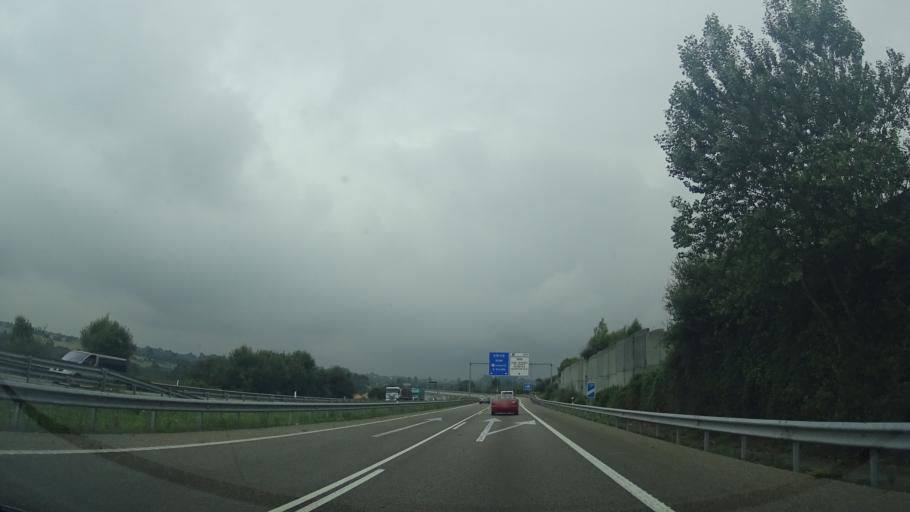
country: ES
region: Asturias
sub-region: Province of Asturias
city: Arriba
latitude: 43.5110
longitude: -5.5631
